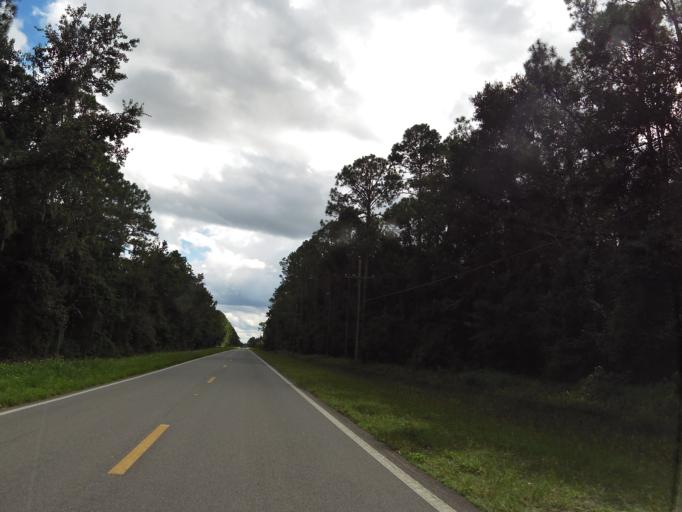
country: US
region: Florida
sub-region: Saint Johns County
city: Saint Augustine
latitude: 29.8736
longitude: -81.4944
